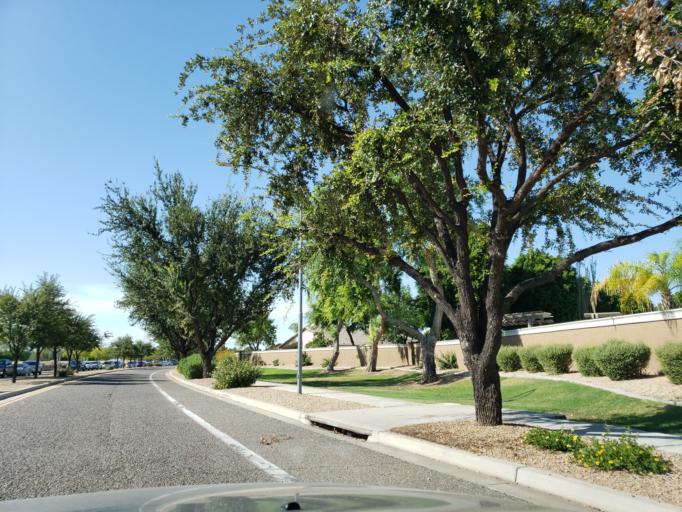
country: US
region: Arizona
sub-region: Maricopa County
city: Peoria
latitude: 33.6642
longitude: -112.1950
